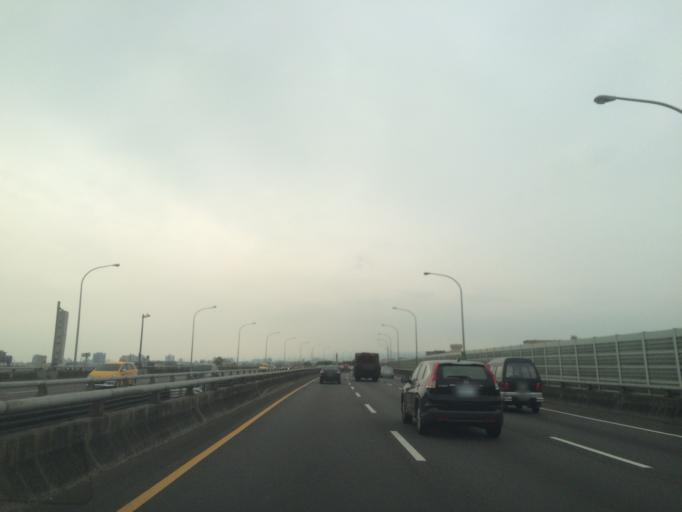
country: TW
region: Taiwan
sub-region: Taichung City
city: Taichung
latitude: 24.1398
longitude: 120.6227
